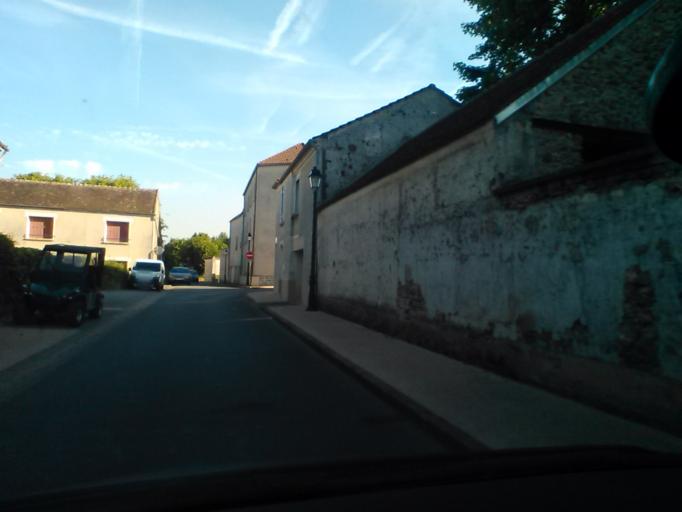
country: FR
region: Ile-de-France
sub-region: Departement de l'Essonne
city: Vert-le-Grand
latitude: 48.5705
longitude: 2.3592
